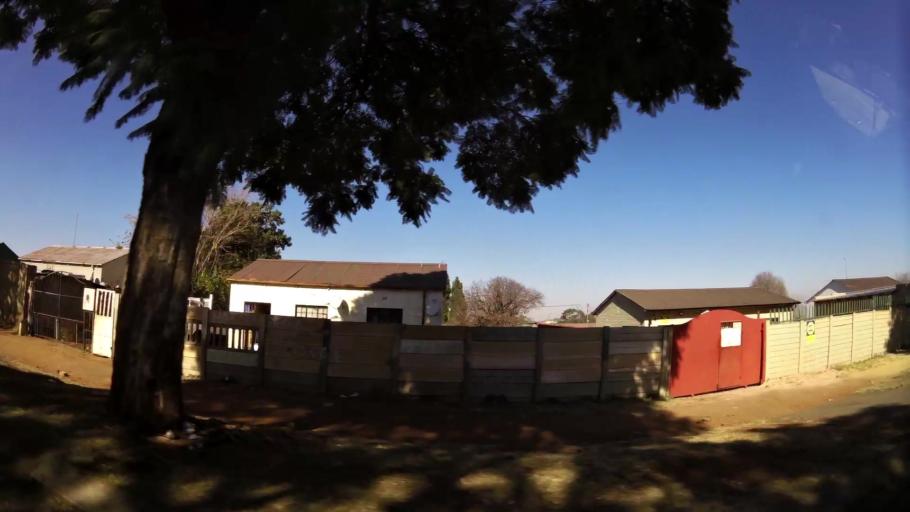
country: ZA
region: Gauteng
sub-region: City of Johannesburg Metropolitan Municipality
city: Johannesburg
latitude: -26.1945
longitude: 27.9804
